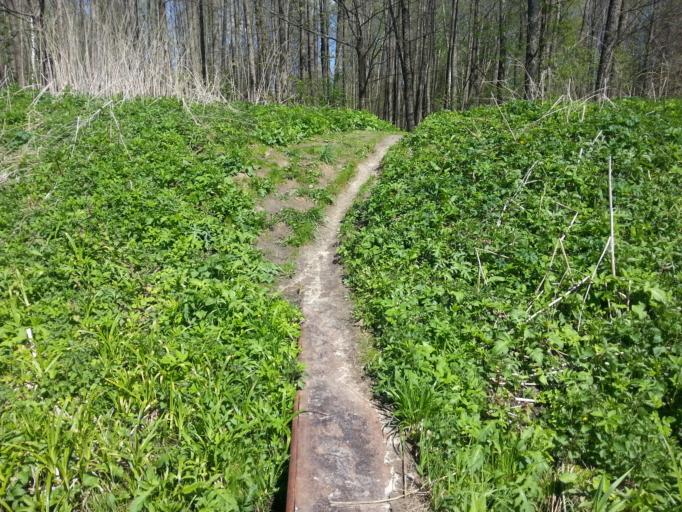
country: BY
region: Mogilev
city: Mstsislaw
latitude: 54.1018
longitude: 31.7494
